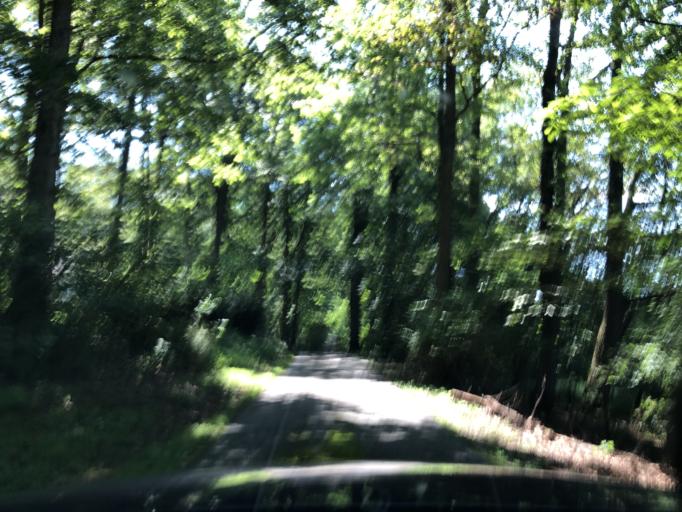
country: US
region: Maryland
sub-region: Carroll County
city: Westminster
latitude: 39.6227
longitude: -77.0039
